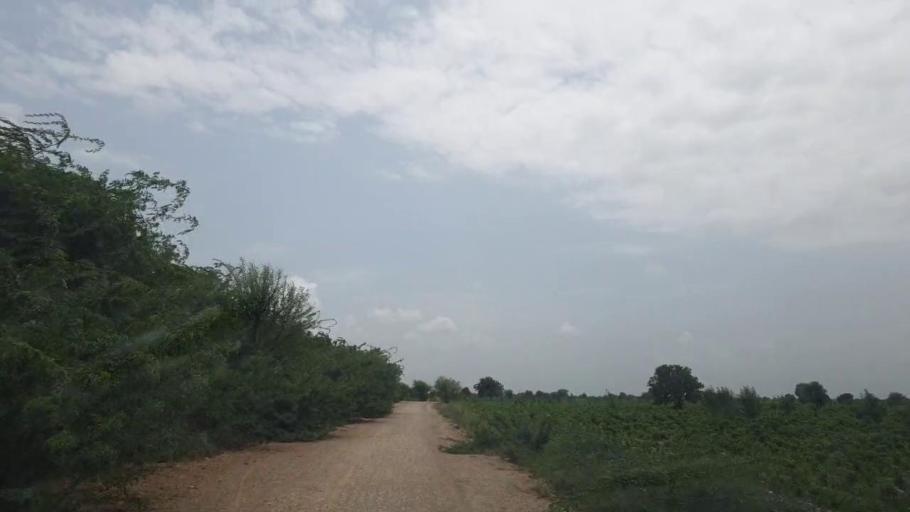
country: PK
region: Sindh
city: Naukot
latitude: 24.9049
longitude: 69.2009
